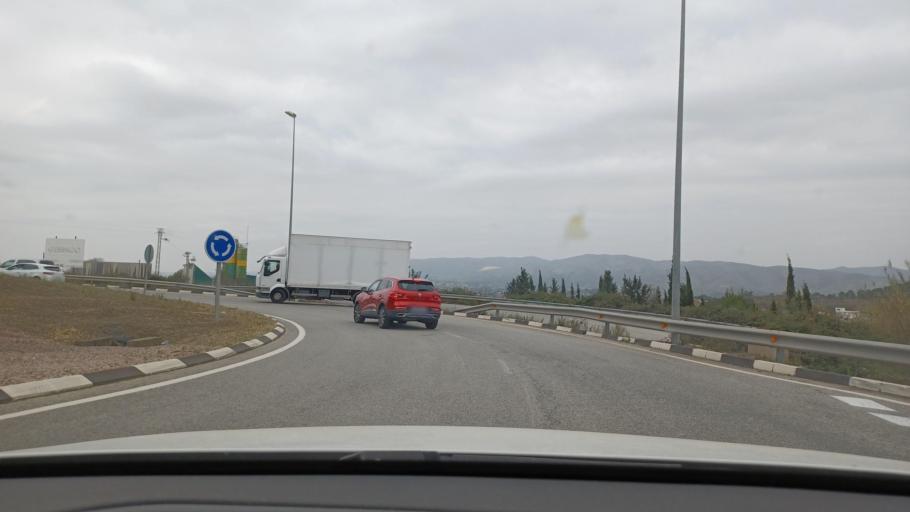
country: ES
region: Valencia
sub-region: Provincia de Valencia
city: Agullent
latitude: 38.8326
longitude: -0.5656
